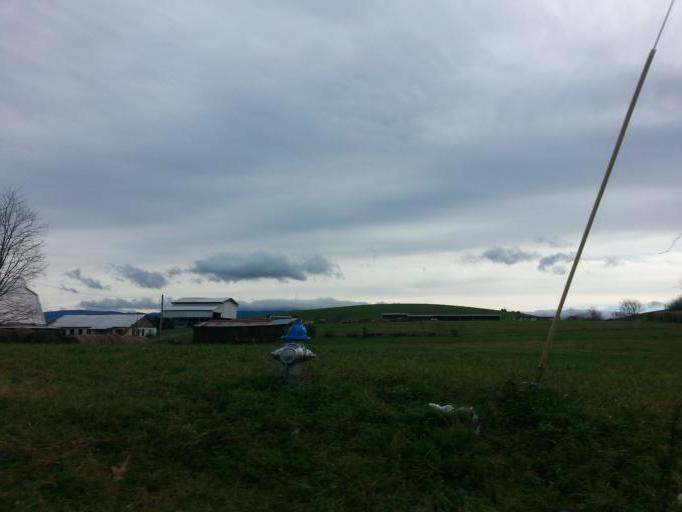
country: US
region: Tennessee
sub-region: Greene County
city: Greeneville
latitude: 36.1423
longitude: -82.8667
